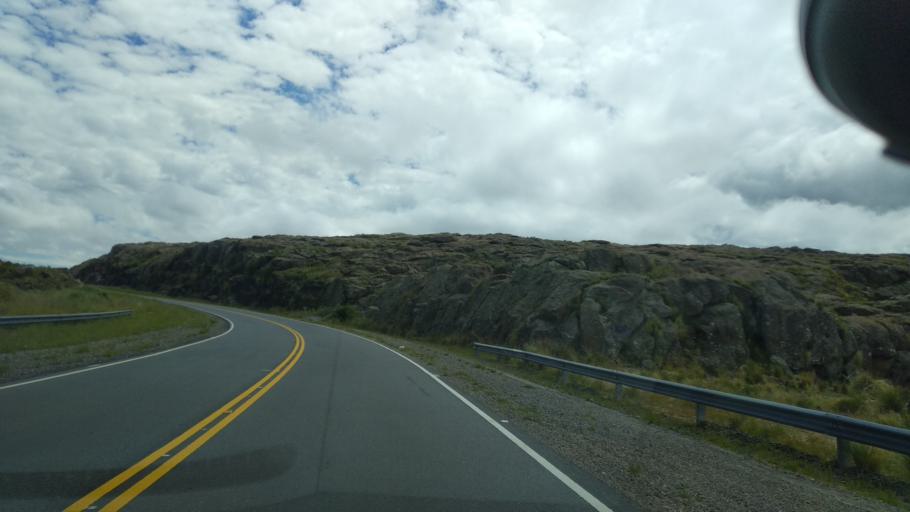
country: AR
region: Cordoba
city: Mina Clavero
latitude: -31.7326
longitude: -64.9007
